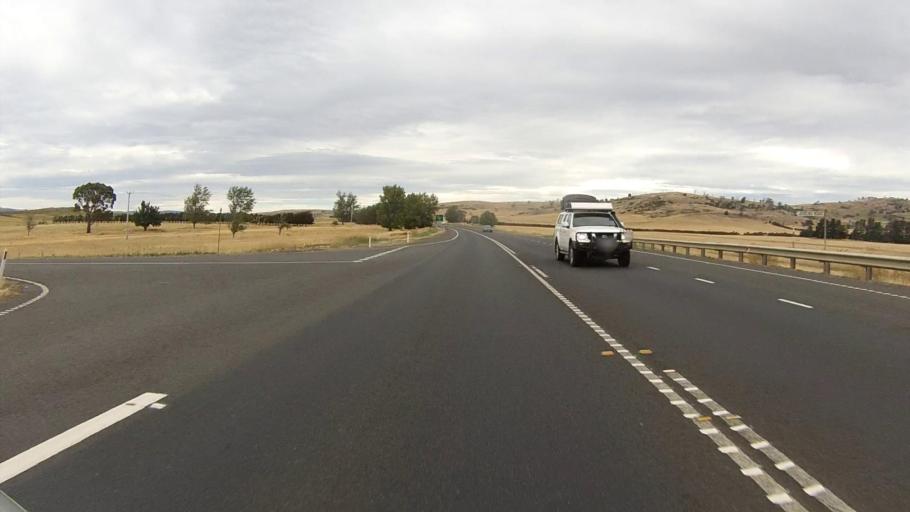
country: AU
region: Tasmania
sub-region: Brighton
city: Bridgewater
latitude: -42.3696
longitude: 147.3336
